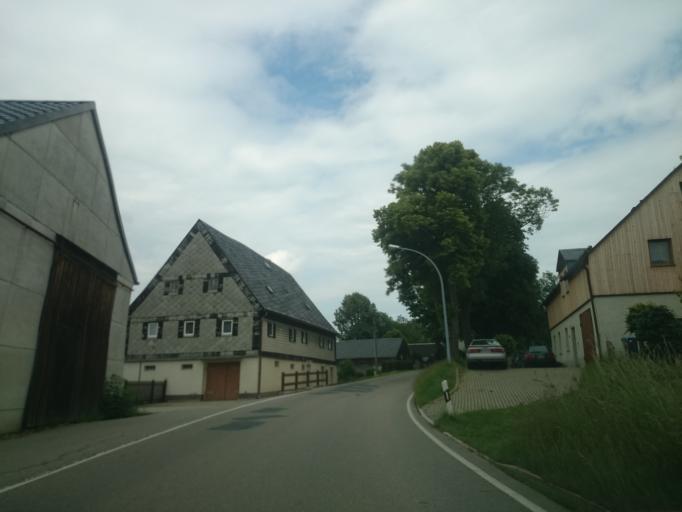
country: DE
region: Saxony
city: Eppendorf
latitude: 50.8175
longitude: 13.2623
